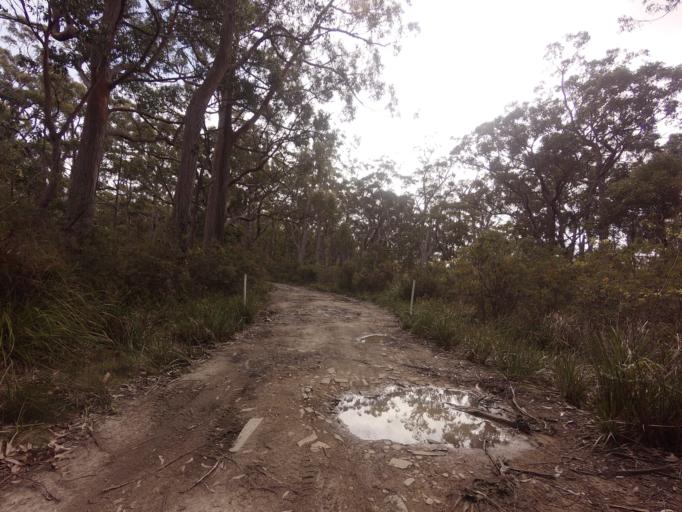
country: AU
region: Tasmania
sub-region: Huon Valley
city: Geeveston
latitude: -43.4677
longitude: 146.9313
